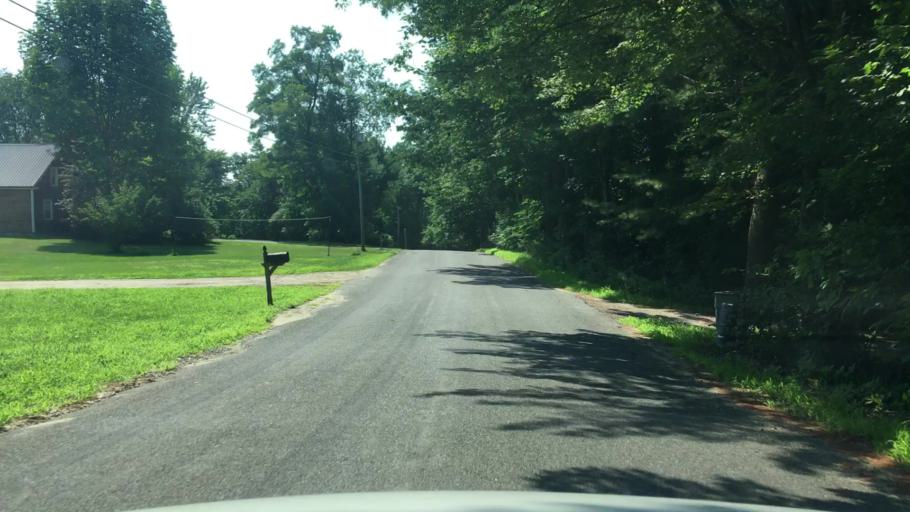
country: US
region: Maine
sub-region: Androscoggin County
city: Greene
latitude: 44.2243
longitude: -70.1051
